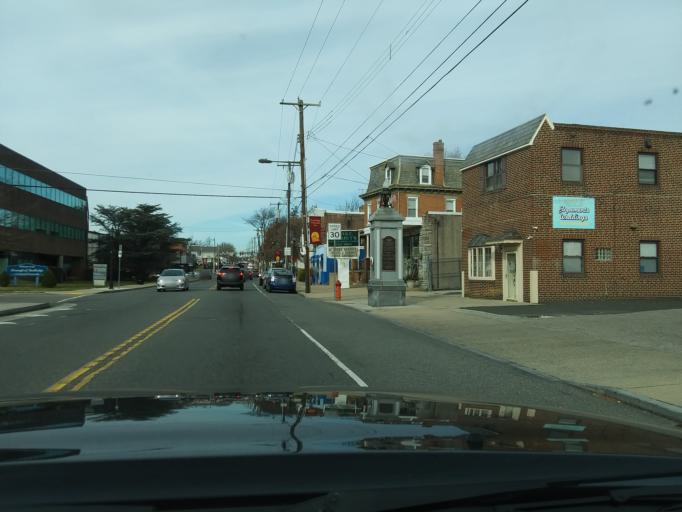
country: US
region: Pennsylvania
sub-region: Montgomery County
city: Rockledge
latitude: 40.0785
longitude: -75.0866
